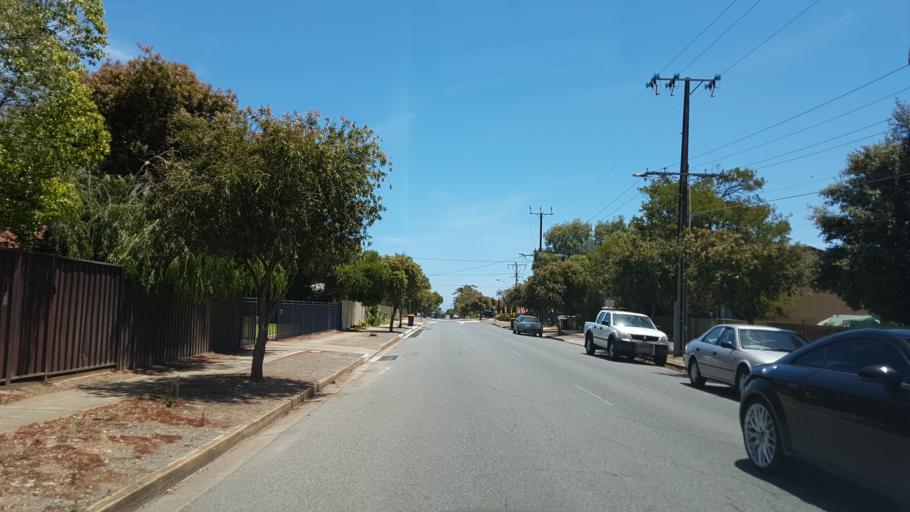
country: AU
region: South Australia
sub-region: Holdfast Bay
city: Seacliff Park
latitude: -35.0254
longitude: 138.5392
